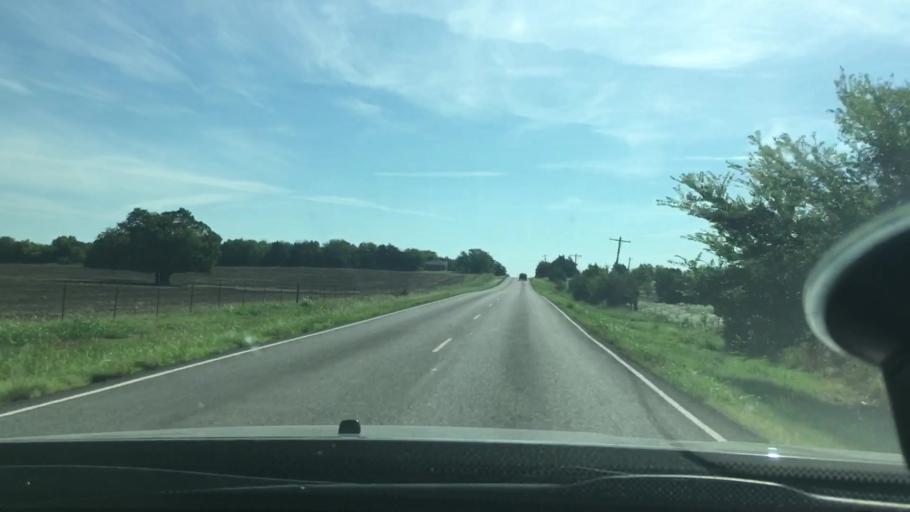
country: US
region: Oklahoma
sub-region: Carter County
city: Ardmore
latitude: 34.3327
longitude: -97.1860
